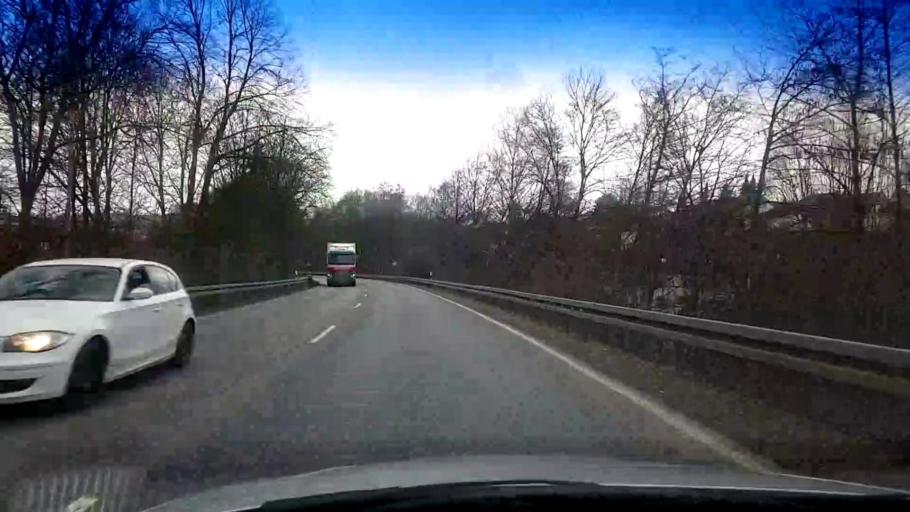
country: DE
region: Bavaria
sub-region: Upper Franconia
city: Kulmbach
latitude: 50.0935
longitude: 11.4517
